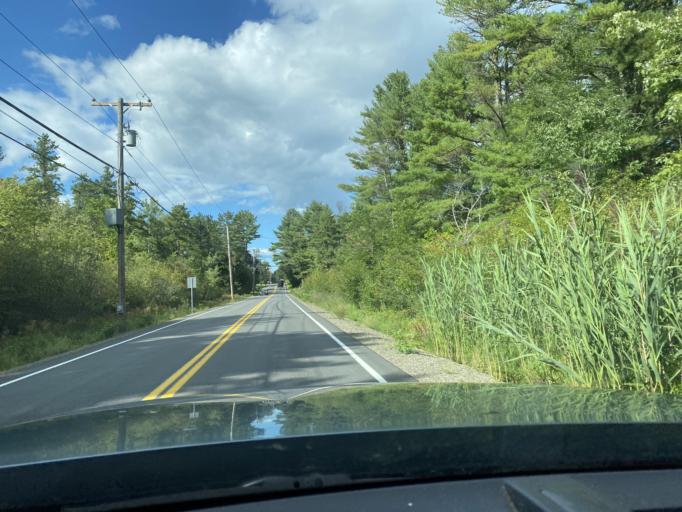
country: US
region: Maine
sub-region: York County
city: York Harbor
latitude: 43.1522
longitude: -70.7119
